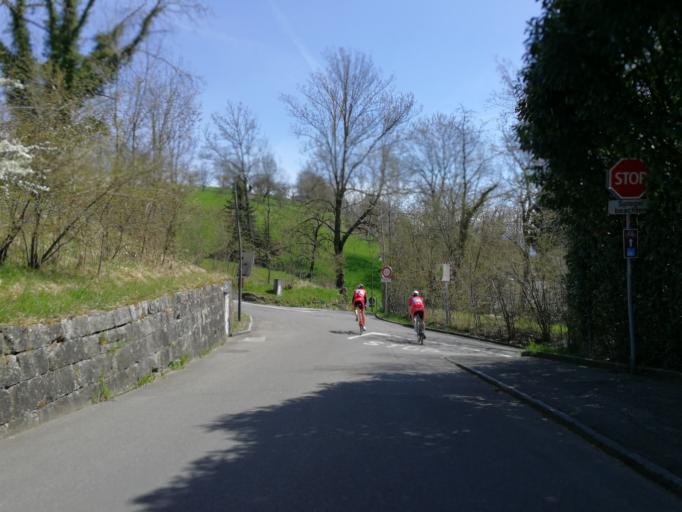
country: CH
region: Zurich
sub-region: Bezirk Meilen
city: Feldmeilen
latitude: 47.2778
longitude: 8.6279
